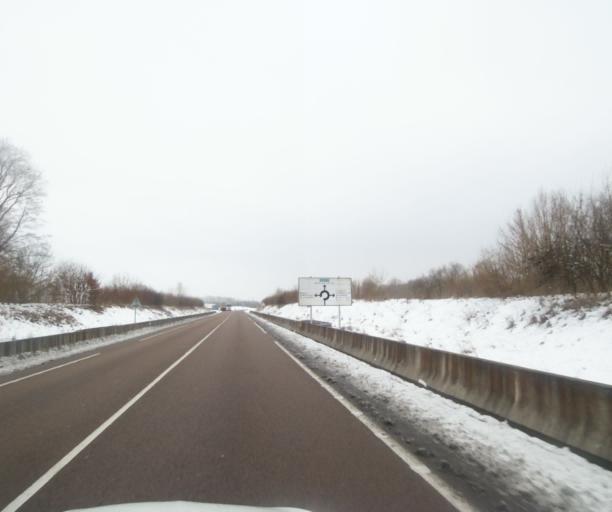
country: FR
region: Champagne-Ardenne
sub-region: Departement de la Haute-Marne
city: Saint-Dizier
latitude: 48.5861
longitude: 4.8899
